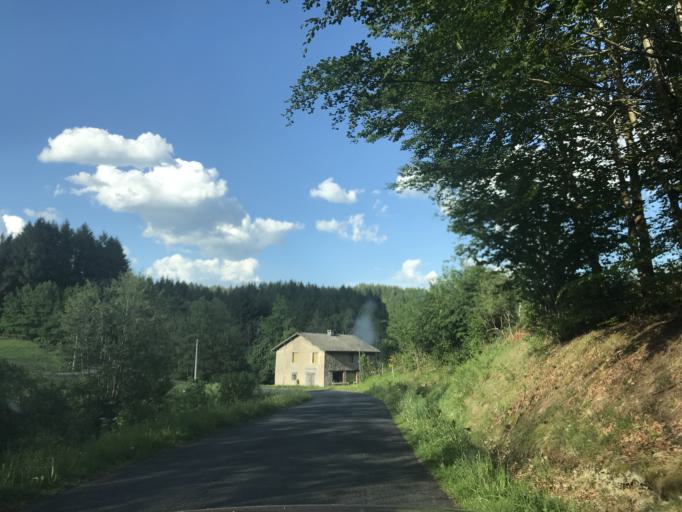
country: FR
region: Auvergne
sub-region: Departement du Puy-de-Dome
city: Job
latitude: 45.7090
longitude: 3.7000
